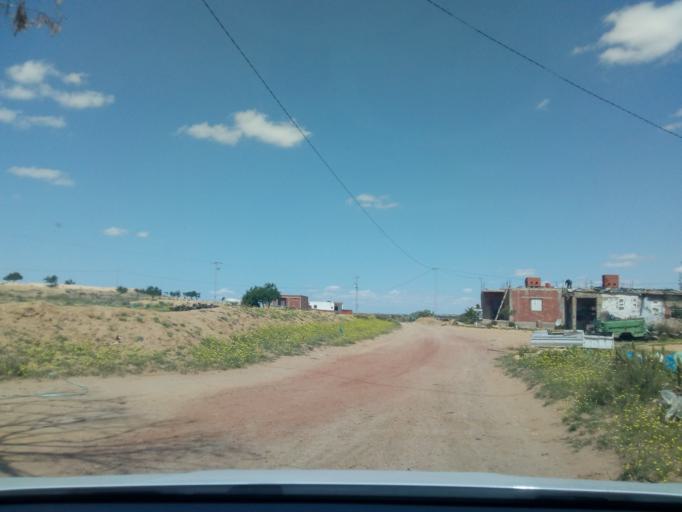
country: TN
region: Safaqis
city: Sfax
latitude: 34.7290
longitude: 10.4984
